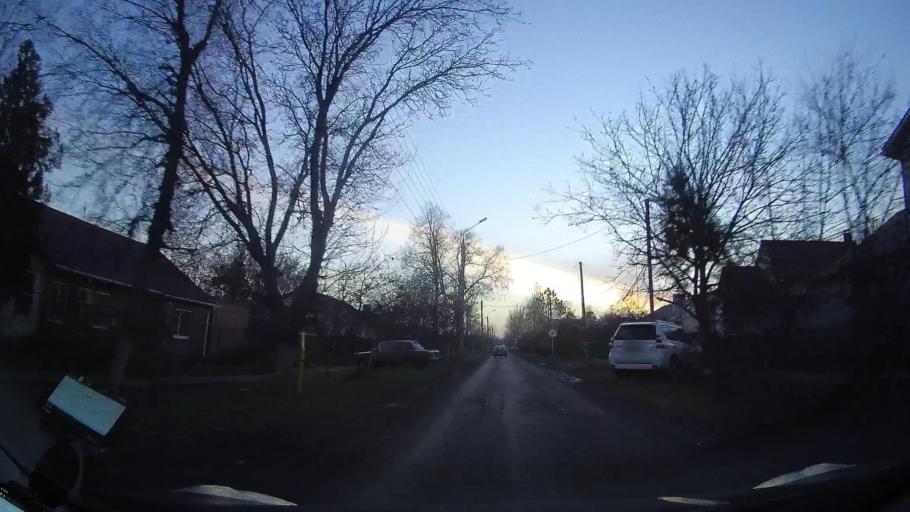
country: RU
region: Rostov
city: Zernograd
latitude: 46.8504
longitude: 40.3073
